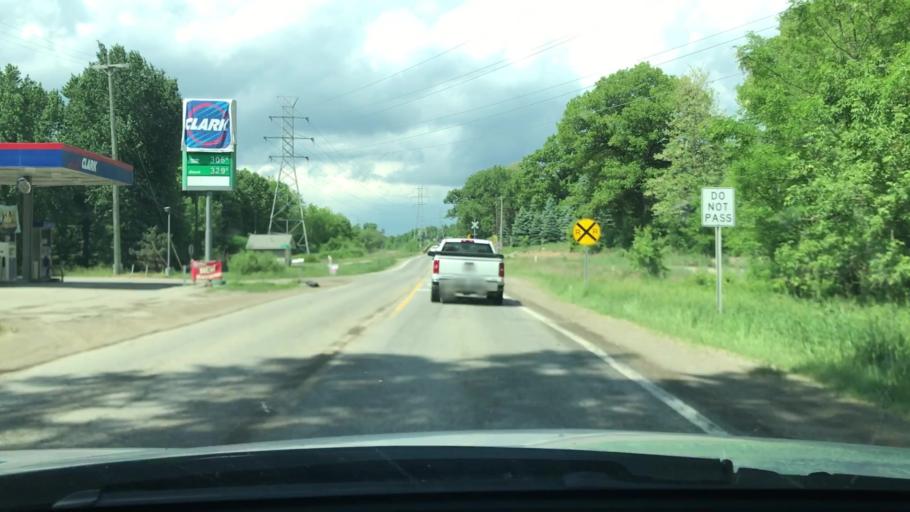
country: US
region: Michigan
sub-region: Oakland County
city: Auburn Hills
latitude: 42.7143
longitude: -83.2852
